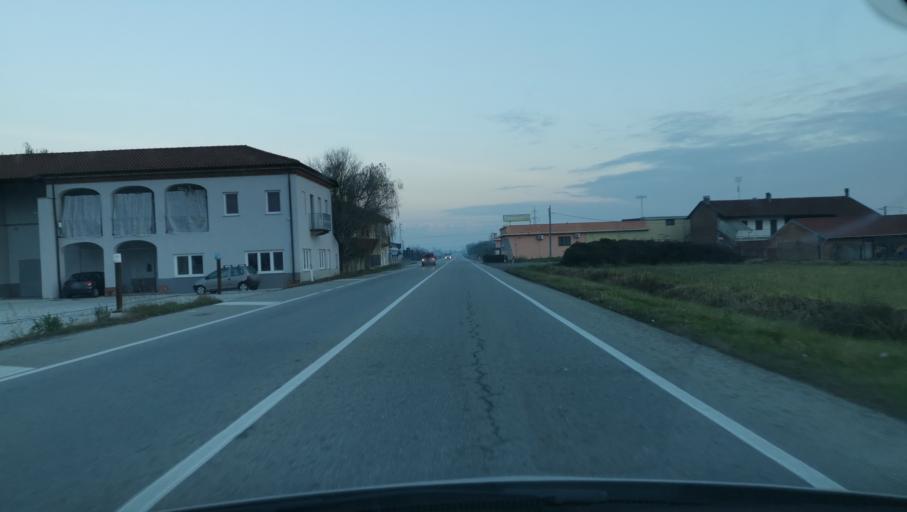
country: IT
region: Piedmont
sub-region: Provincia di Torino
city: Chivasso
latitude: 45.2185
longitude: 7.8905
